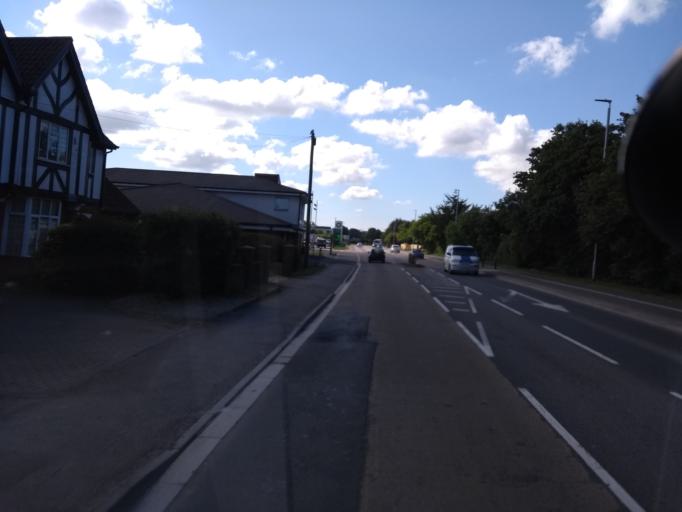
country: GB
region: England
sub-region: Somerset
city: Bridgwater
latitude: 51.1149
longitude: -2.9961
